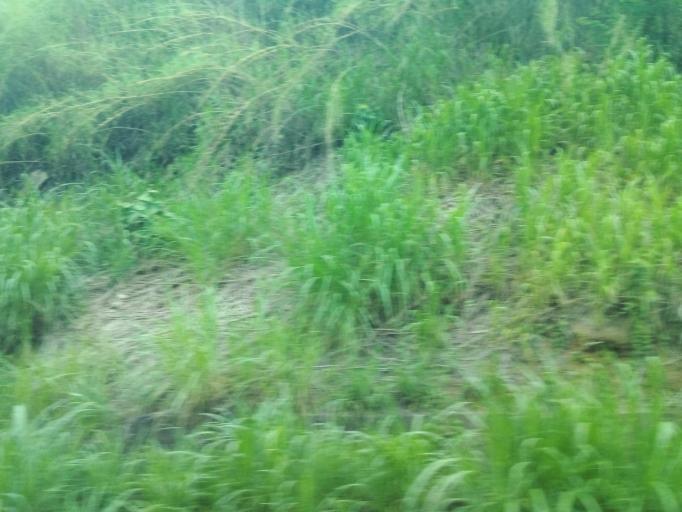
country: BR
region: Minas Gerais
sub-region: Nova Era
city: Nova Era
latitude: -19.7313
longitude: -43.0057
